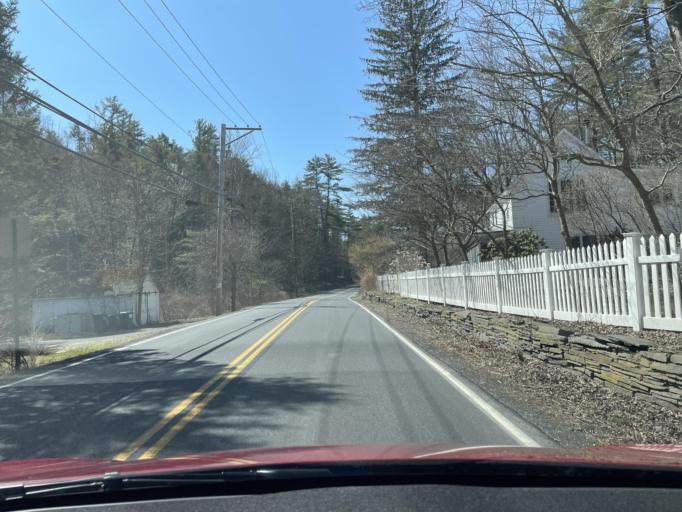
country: US
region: New York
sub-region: Ulster County
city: Woodstock
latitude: 42.0359
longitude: -74.1737
